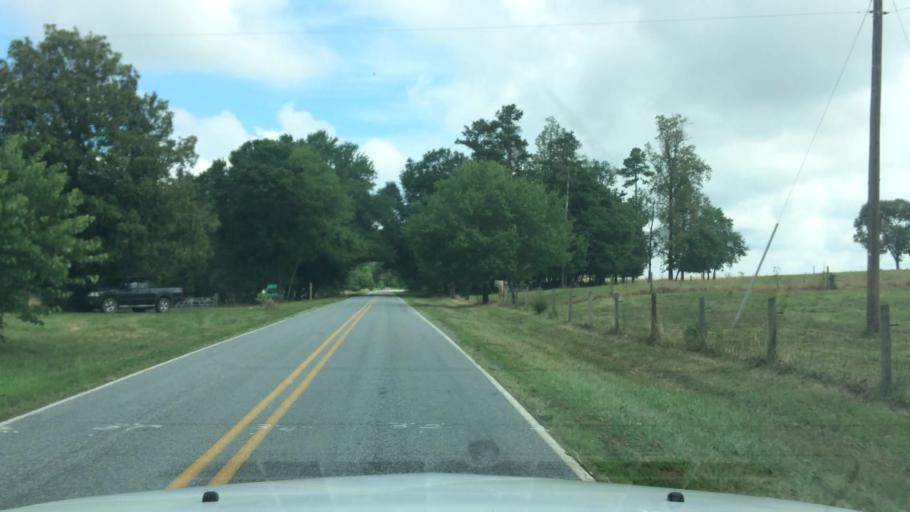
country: US
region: North Carolina
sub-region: Yadkin County
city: Jonesville
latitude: 36.1115
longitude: -80.8565
